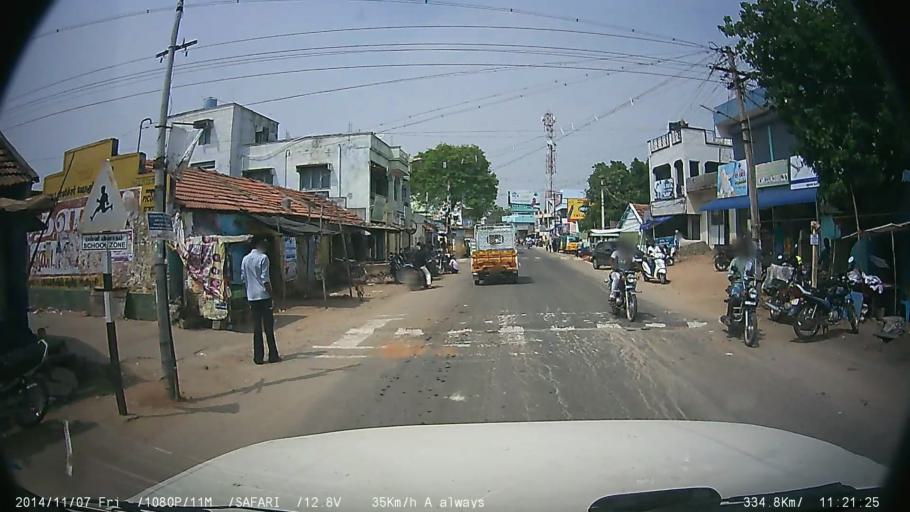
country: IN
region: Tamil Nadu
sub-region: Tiruppur
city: Tiruppur
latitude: 11.1020
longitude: 77.2736
